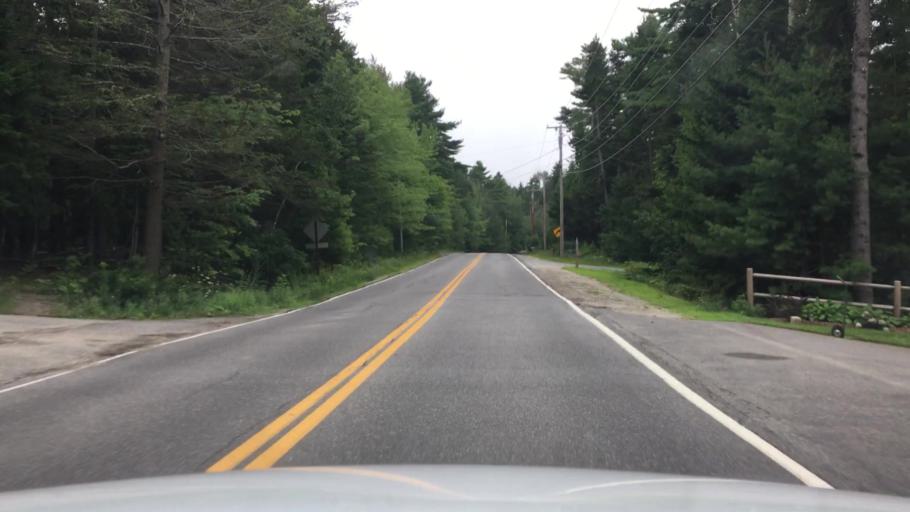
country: US
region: Maine
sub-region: Cumberland County
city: Harpswell Center
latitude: 43.7760
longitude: -69.9583
